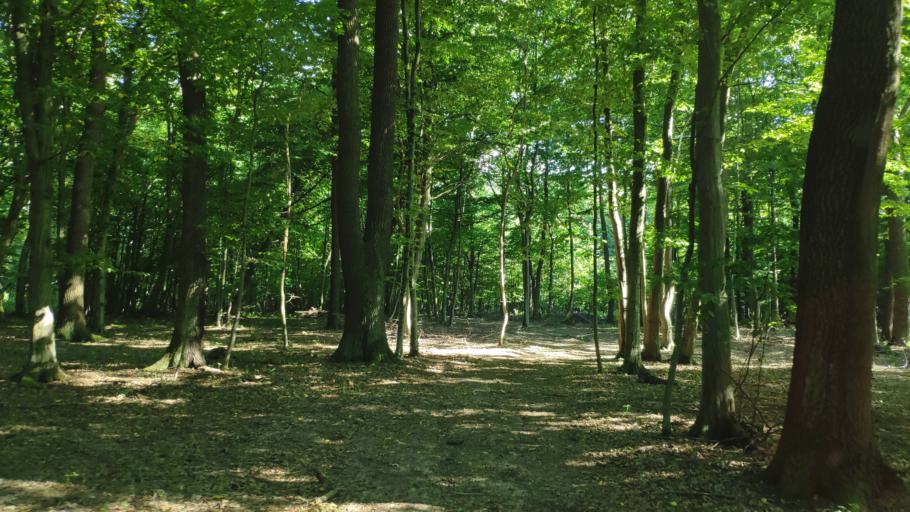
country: SK
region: Presovsky
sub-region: Okres Presov
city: Presov
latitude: 48.9057
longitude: 21.2920
